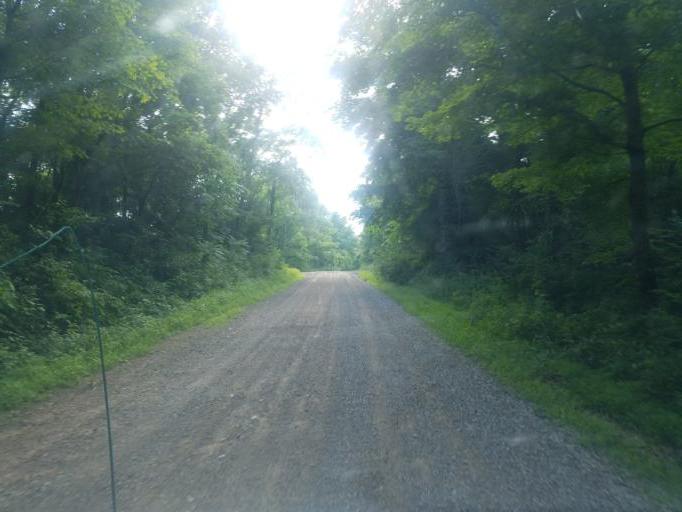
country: US
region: Ohio
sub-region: Knox County
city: Oak Hill
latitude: 40.3875
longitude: -82.1739
